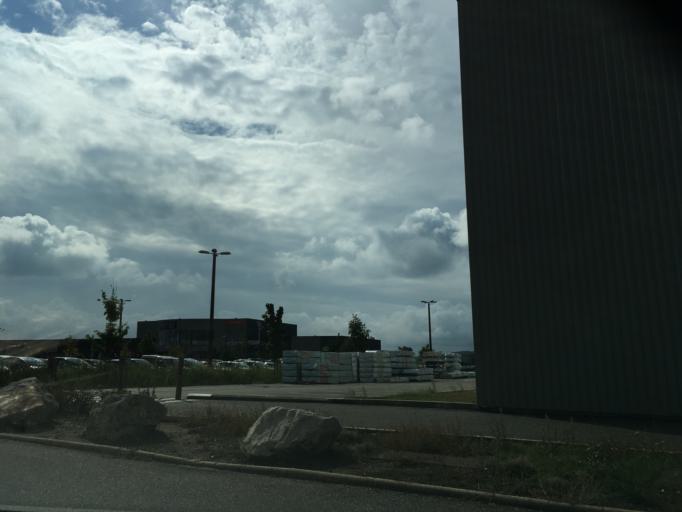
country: FR
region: Aquitaine
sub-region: Departement du Lot-et-Garonne
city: Boe
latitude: 44.1755
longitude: 0.6321
